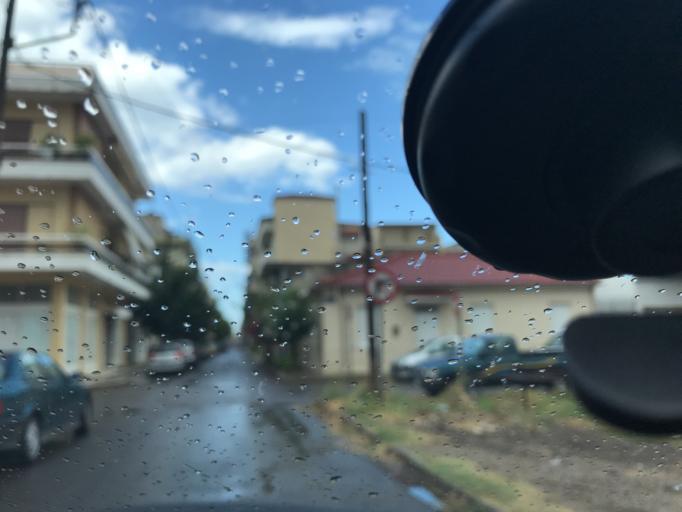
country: GR
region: West Greece
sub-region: Nomos Ileias
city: Pyrgos
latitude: 37.6761
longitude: 21.4379
